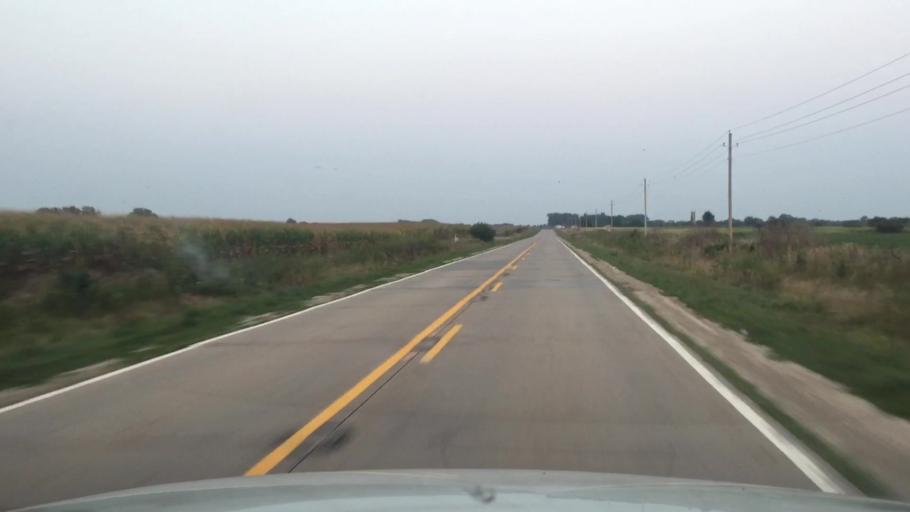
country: US
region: Iowa
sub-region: Clarke County
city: Osceola
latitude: 41.1875
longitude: -93.6904
